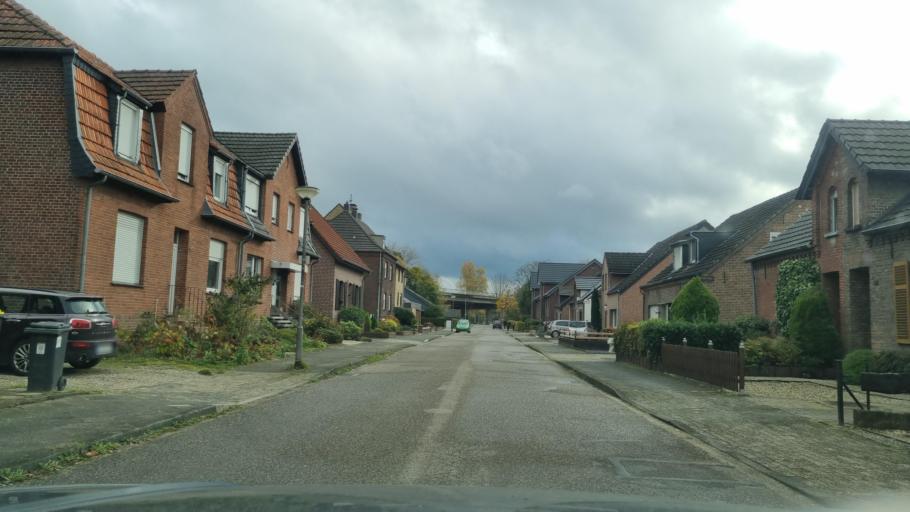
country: DE
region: North Rhine-Westphalia
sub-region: Regierungsbezirk Dusseldorf
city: Kleve
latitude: 51.7990
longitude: 6.1329
